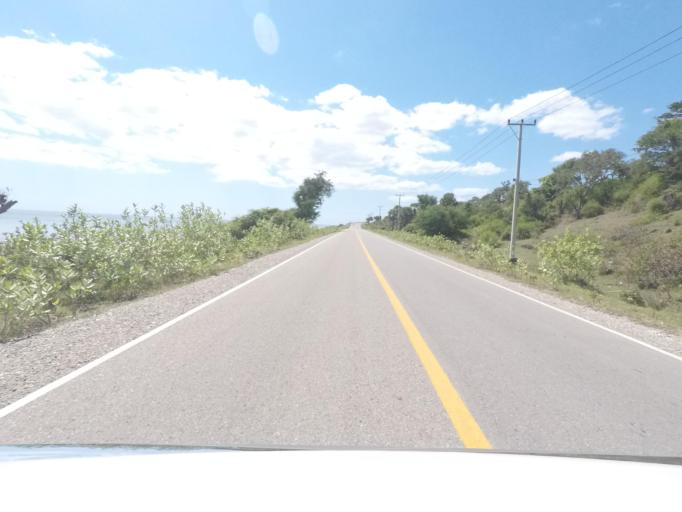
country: TL
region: Lautem
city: Lospalos
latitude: -8.3721
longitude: 126.8778
